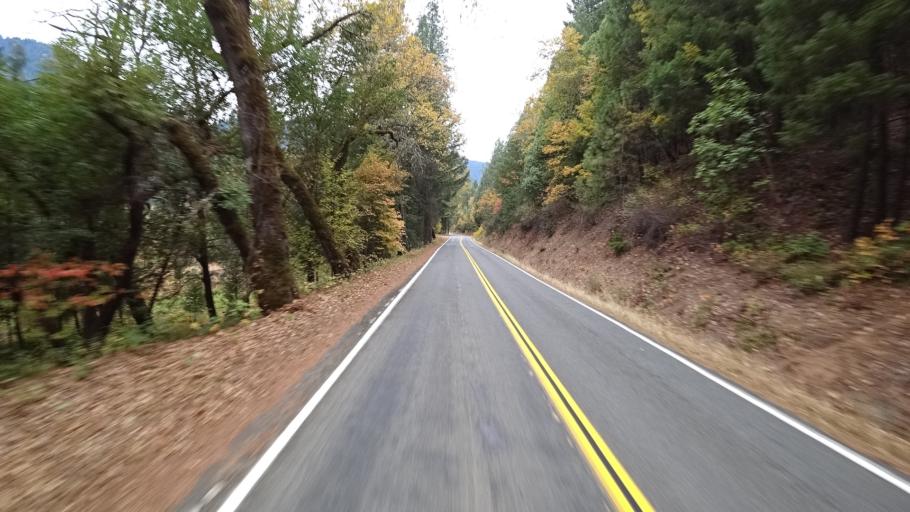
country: US
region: California
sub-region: Siskiyou County
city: Happy Camp
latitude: 41.8586
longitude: -123.3966
